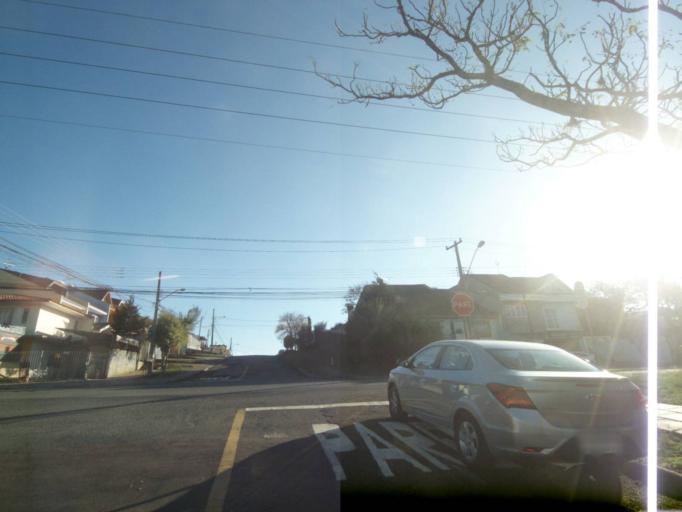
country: BR
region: Parana
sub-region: Curitiba
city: Curitiba
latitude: -25.3828
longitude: -49.2507
